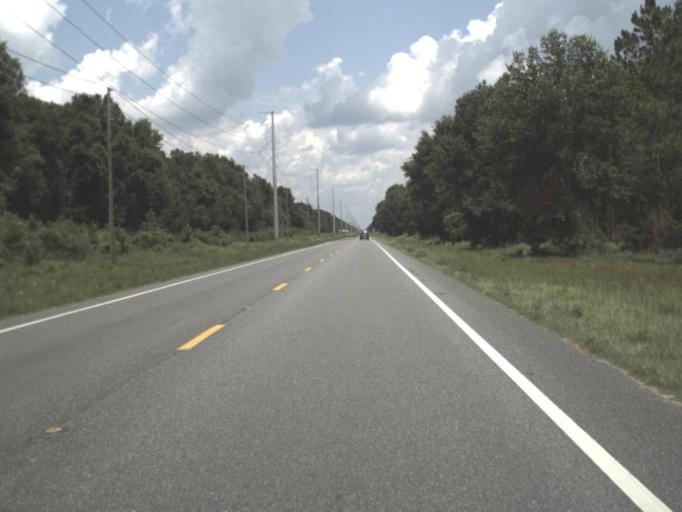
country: US
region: Florida
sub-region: Gilchrist County
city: Trenton
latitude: 29.6125
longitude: -82.8877
